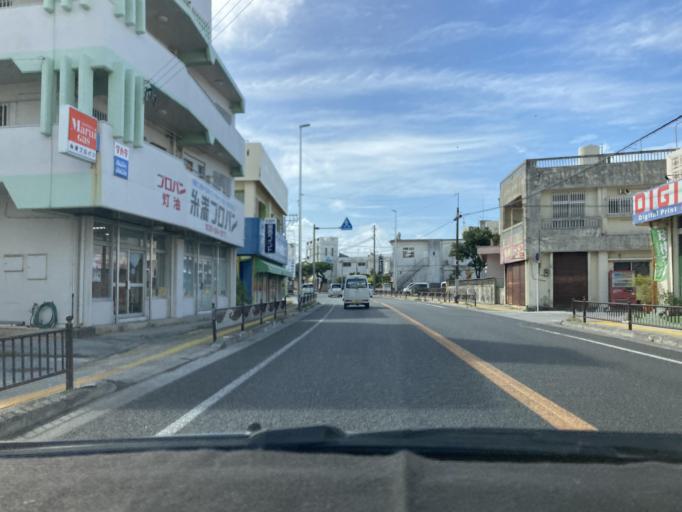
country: JP
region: Okinawa
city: Itoman
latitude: 26.1346
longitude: 127.6697
